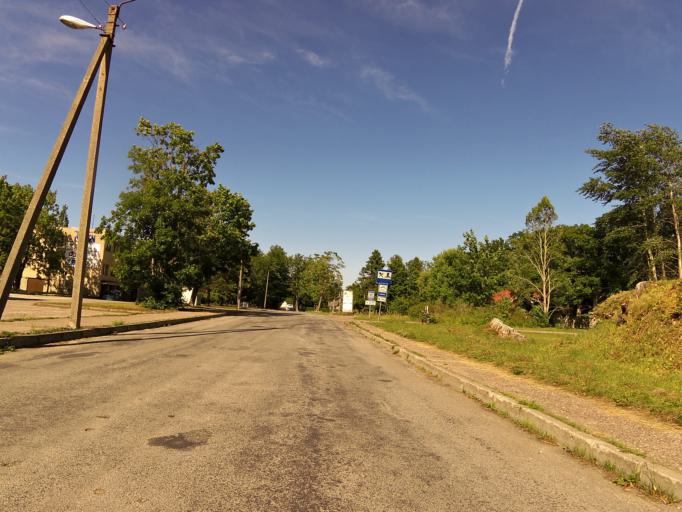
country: EE
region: Hiiumaa
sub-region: Kaerdla linn
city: Kardla
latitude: 59.0024
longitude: 22.7485
